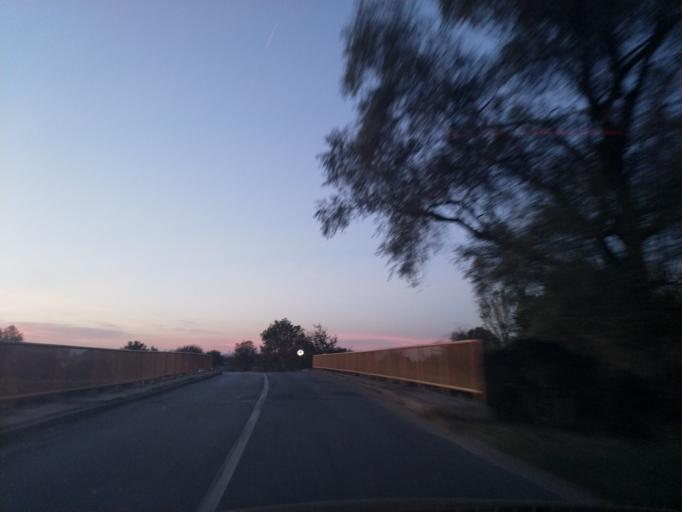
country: RS
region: Central Serbia
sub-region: Pomoravski Okrug
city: Svilajnac
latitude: 44.2288
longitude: 21.1452
